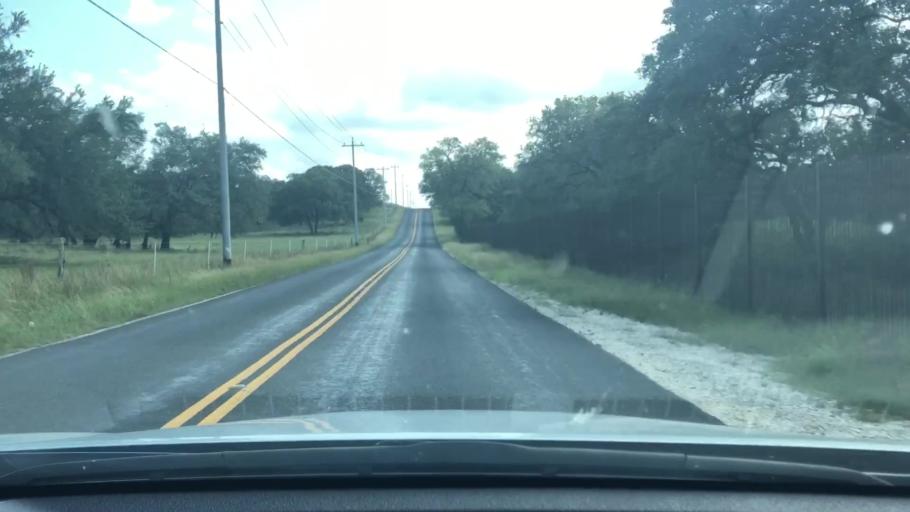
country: US
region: Texas
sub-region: Bexar County
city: Fair Oaks Ranch
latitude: 29.7788
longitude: -98.6265
